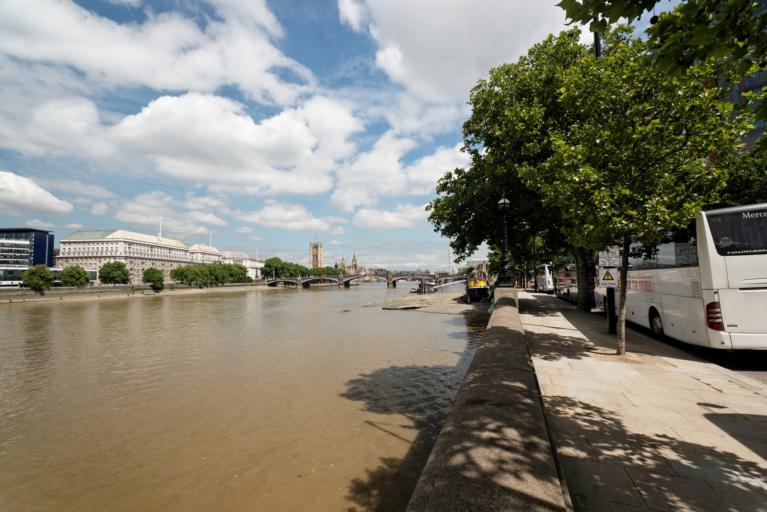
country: GB
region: England
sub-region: Greater London
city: City of Westminster
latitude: 51.4911
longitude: -0.1225
